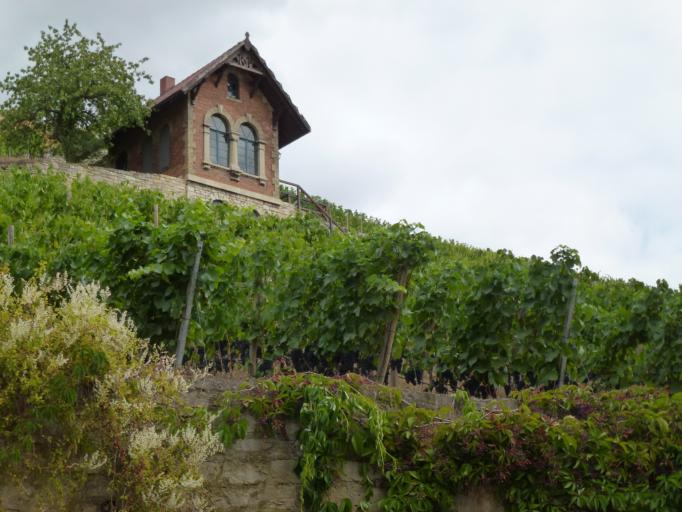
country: DE
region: Saxony-Anhalt
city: Freyburg
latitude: 51.2125
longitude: 11.7718
